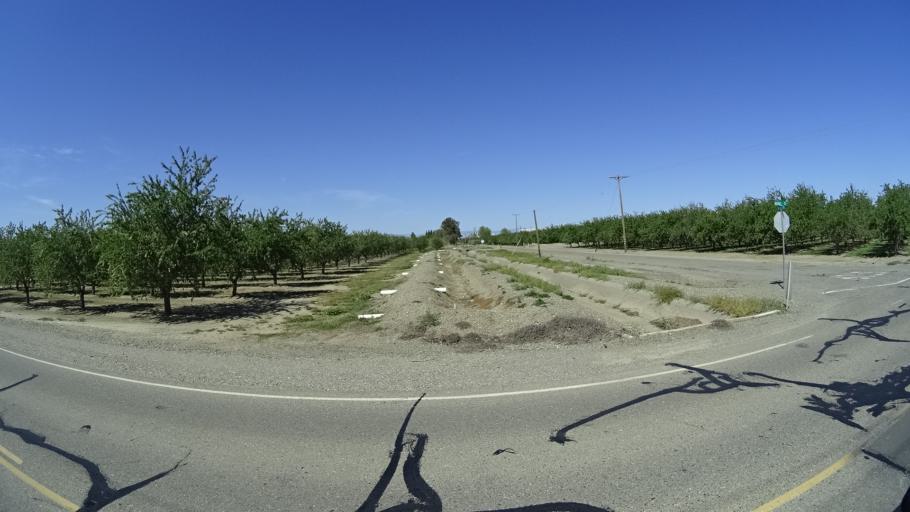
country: US
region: California
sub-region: Glenn County
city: Hamilton City
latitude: 39.7318
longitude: -122.1043
